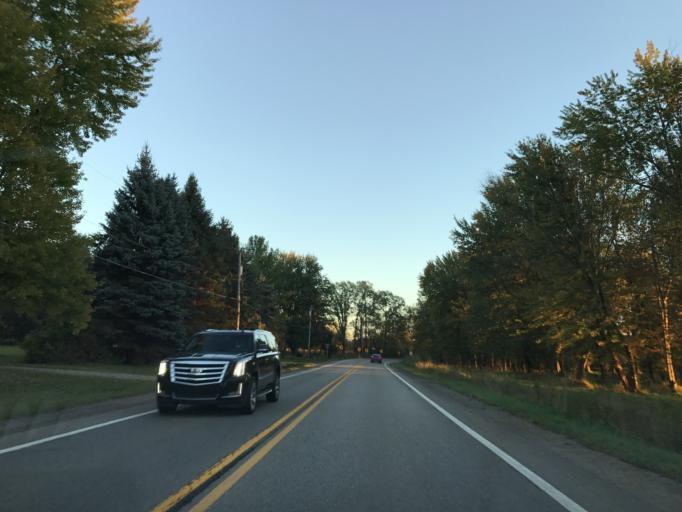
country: US
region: Michigan
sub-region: Oakland County
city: South Lyon
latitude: 42.4890
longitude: -83.6138
